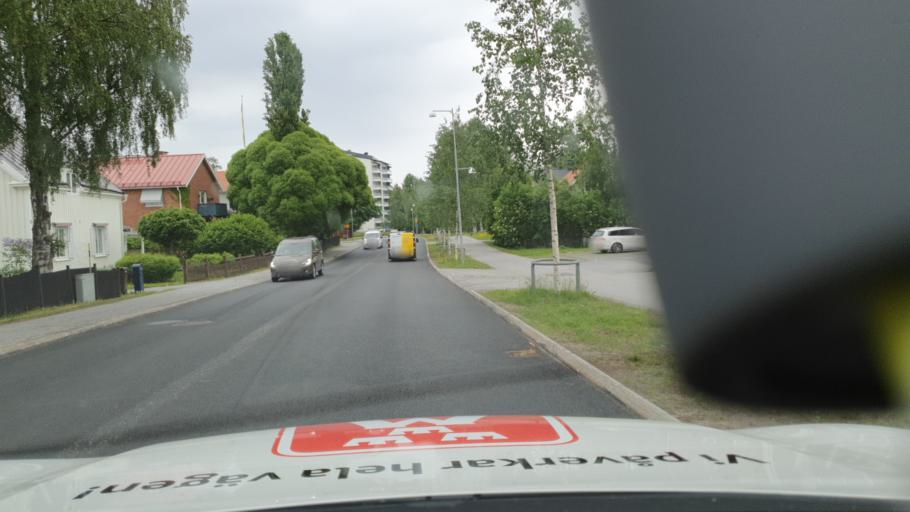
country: SE
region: Vaesterbotten
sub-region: Umea Kommun
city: Umea
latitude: 63.8325
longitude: 20.2231
